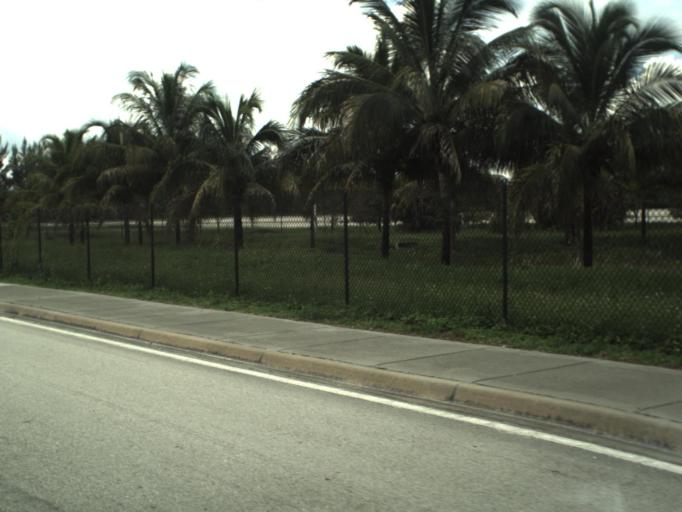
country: US
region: Florida
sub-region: Miami-Dade County
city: Tamiami
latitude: 25.7776
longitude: -80.4173
